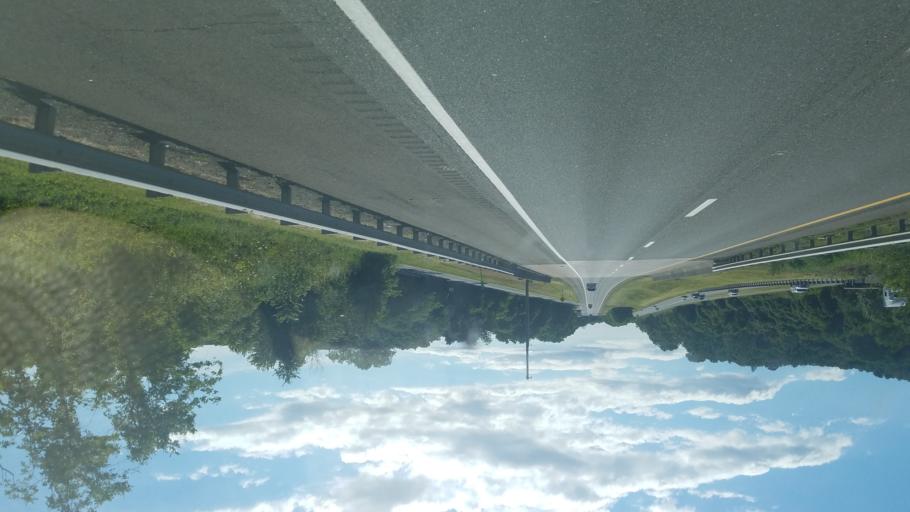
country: US
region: Virginia
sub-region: Warren County
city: Apple Mountain Lake
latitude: 38.9070
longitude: -77.9987
